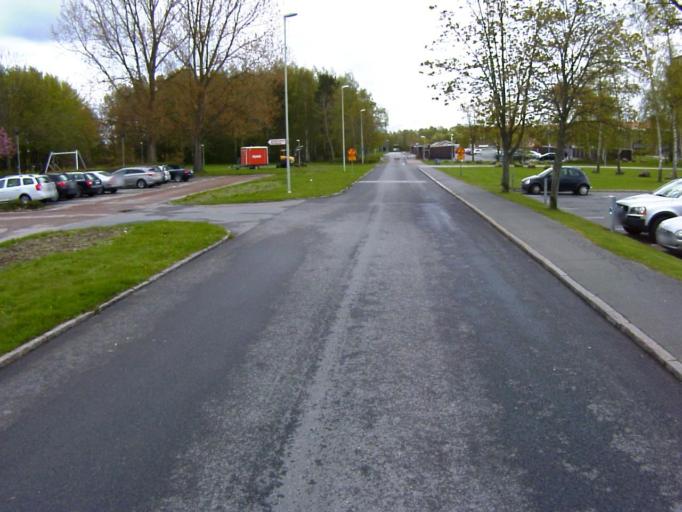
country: SE
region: Skane
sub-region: Kristianstads Kommun
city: Kristianstad
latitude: 56.0445
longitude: 14.1828
